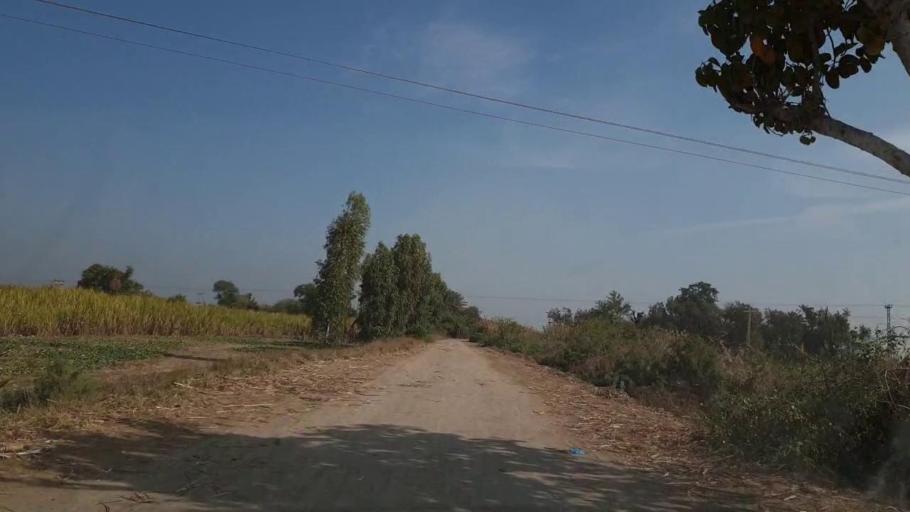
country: PK
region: Sindh
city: Mirpur Khas
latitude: 25.5091
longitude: 69.1104
